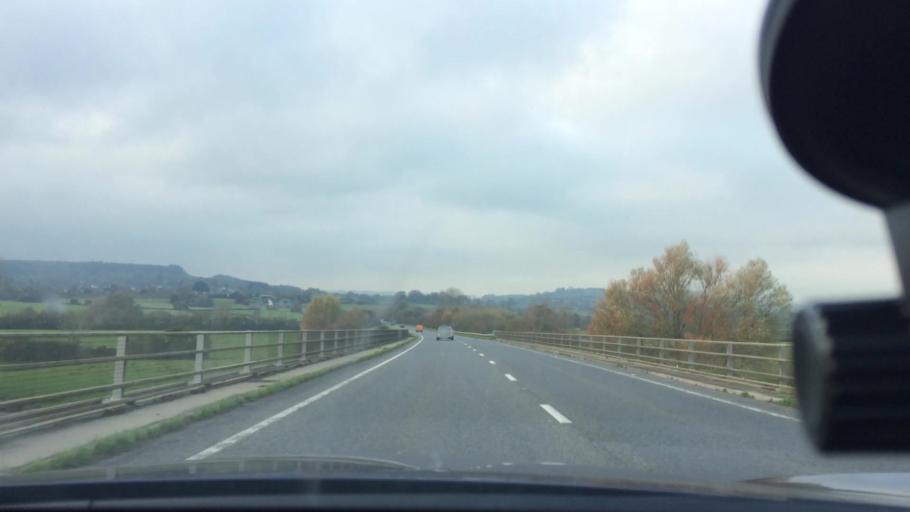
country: GB
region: England
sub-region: Devon
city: Axminster
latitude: 50.7739
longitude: -3.0125
